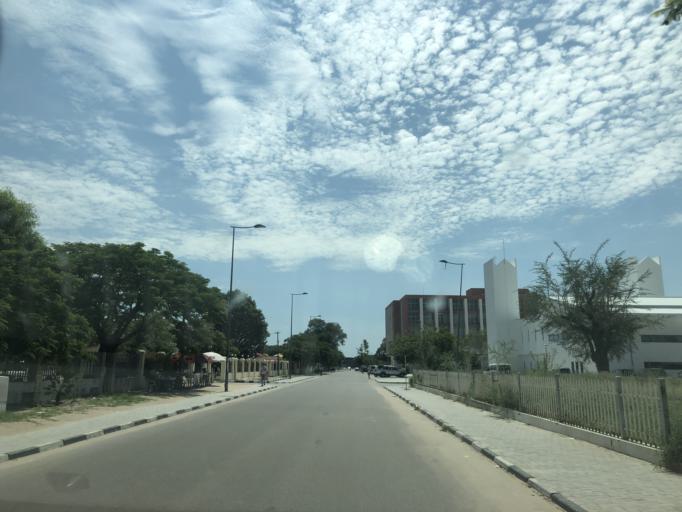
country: AO
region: Cunene
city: Ondjiva
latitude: -17.0664
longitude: 15.7256
